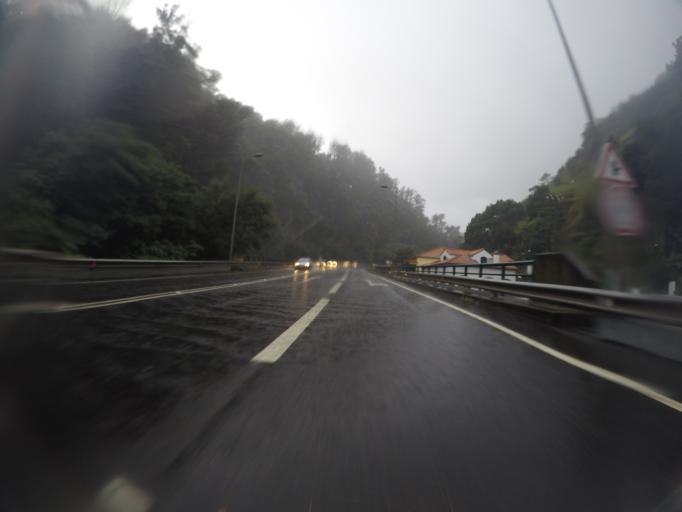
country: PT
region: Madeira
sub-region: Machico
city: Machico
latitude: 32.7348
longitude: -16.8036
